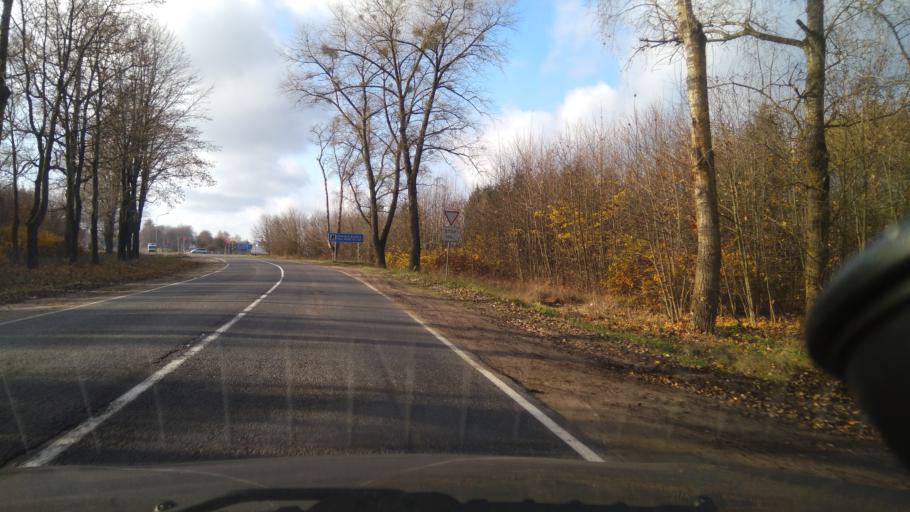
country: BY
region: Minsk
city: Slutsk
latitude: 53.2210
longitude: 27.5538
